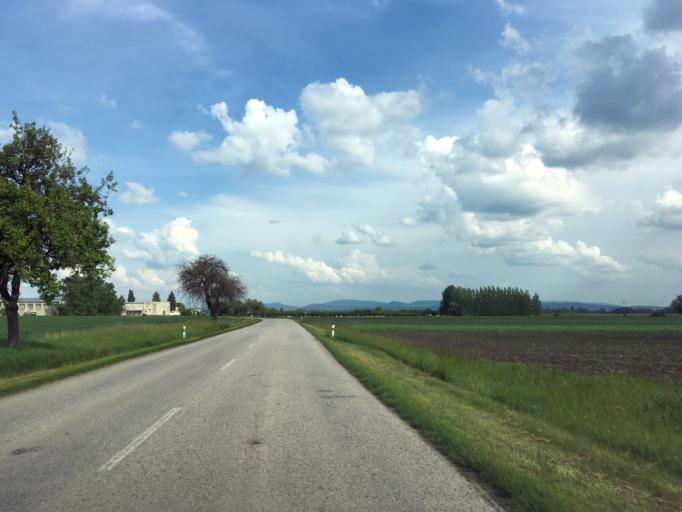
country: HU
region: Komarom-Esztergom
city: Almasfuzito
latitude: 47.7896
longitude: 18.2606
